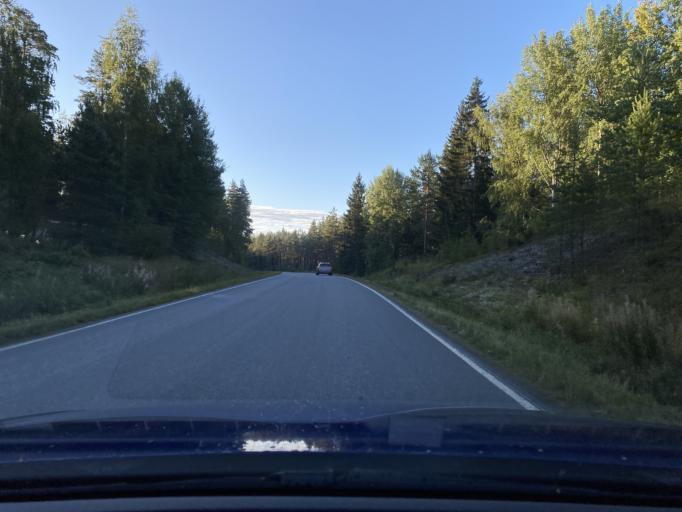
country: FI
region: Haeme
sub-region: Forssa
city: Tammela
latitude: 60.9336
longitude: 23.7898
